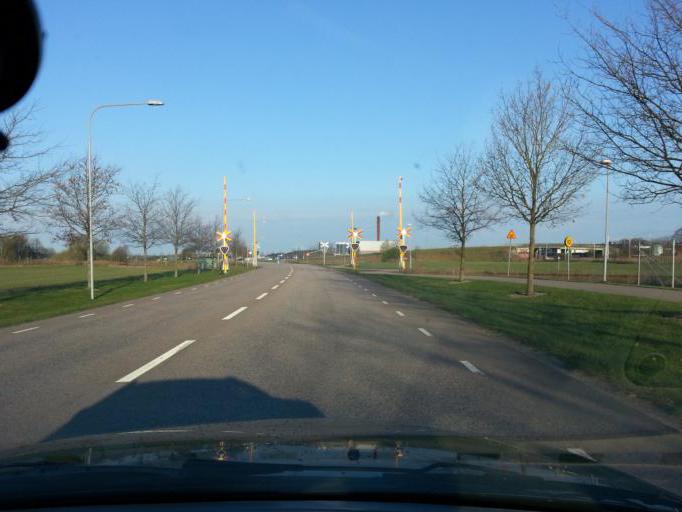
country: SE
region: Skane
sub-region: Klippans Kommun
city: Klippan
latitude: 56.1292
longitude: 13.1425
